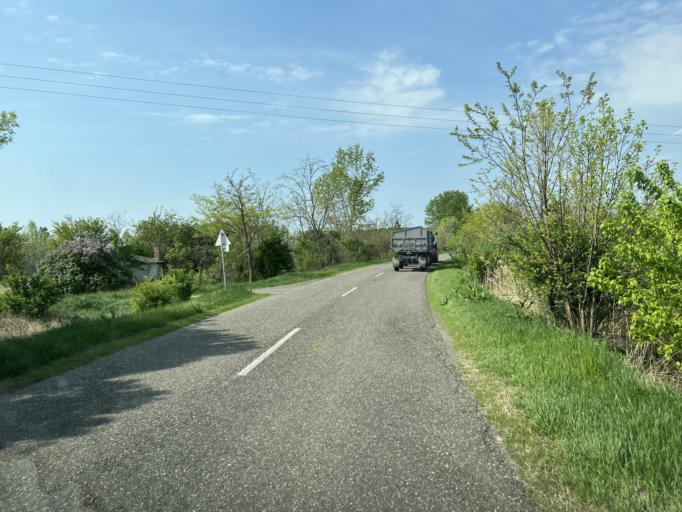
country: HU
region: Pest
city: Tortel
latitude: 47.0917
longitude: 19.8890
